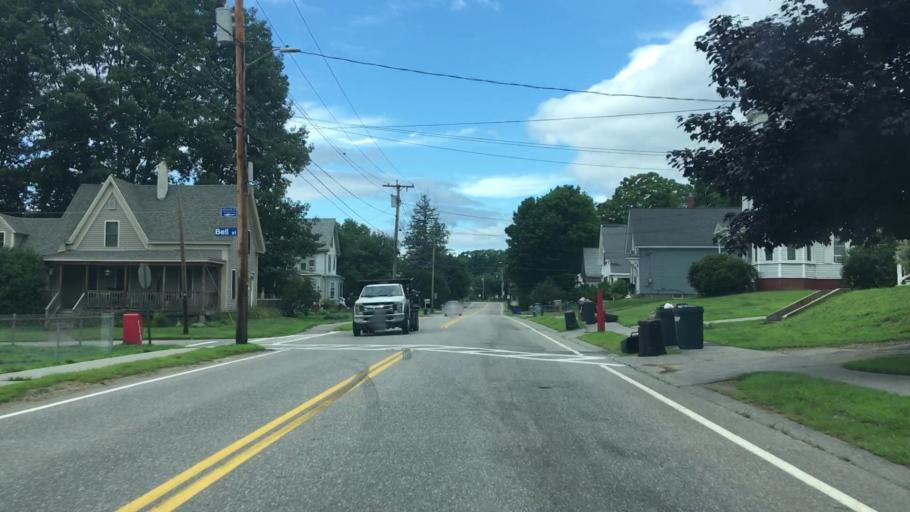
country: US
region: New Hampshire
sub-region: Belknap County
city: Laconia
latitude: 43.5545
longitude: -71.4689
